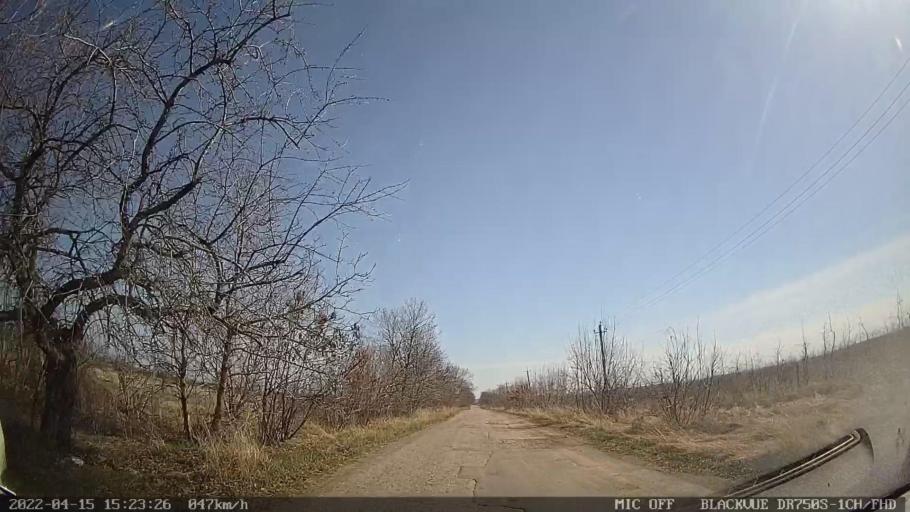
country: MD
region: Raionul Ocnita
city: Otaci
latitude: 48.3750
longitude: 27.9193
